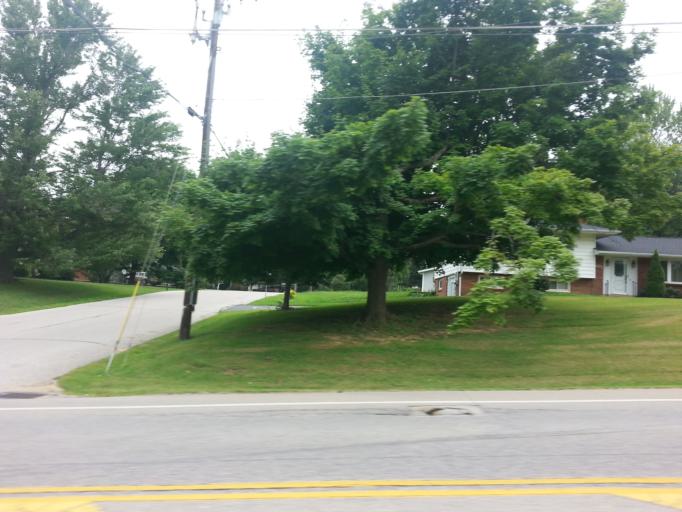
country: US
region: Ohio
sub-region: Brown County
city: Mount Orab
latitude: 39.0208
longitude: -83.9239
